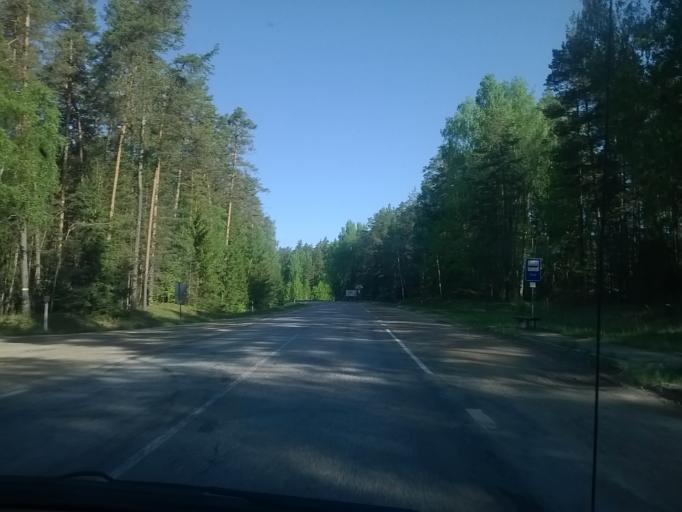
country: LV
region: Strenci
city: Seda
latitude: 57.6281
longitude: 25.7423
